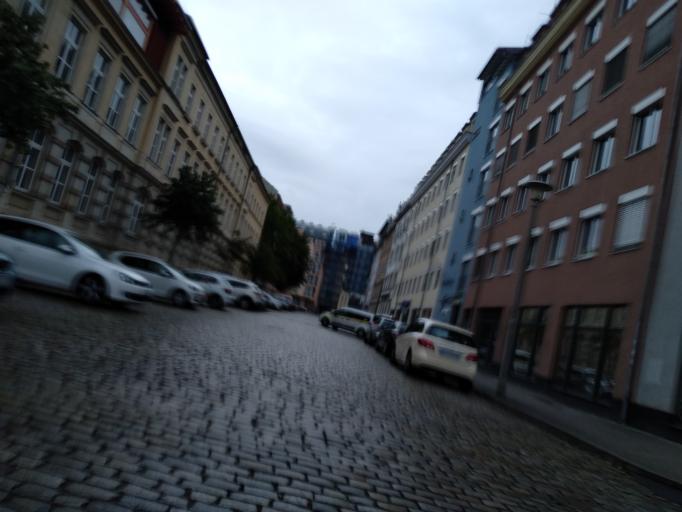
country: DE
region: Saxony
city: Albertstadt
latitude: 51.0583
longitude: 13.7695
